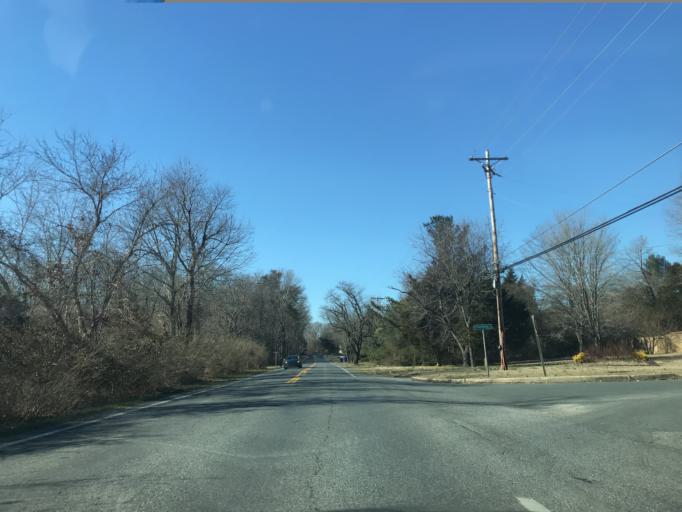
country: US
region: Maryland
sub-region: Charles County
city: Saint Charles
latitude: 38.5912
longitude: -76.9729
